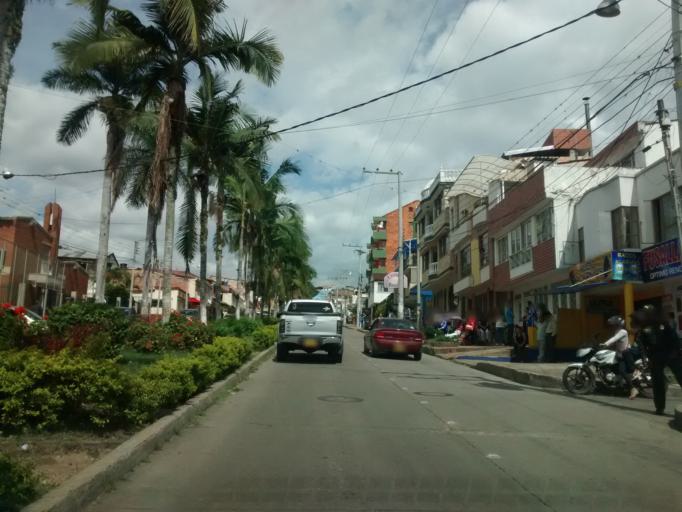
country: CO
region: Cundinamarca
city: Fusagasuga
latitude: 4.3356
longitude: -74.3654
